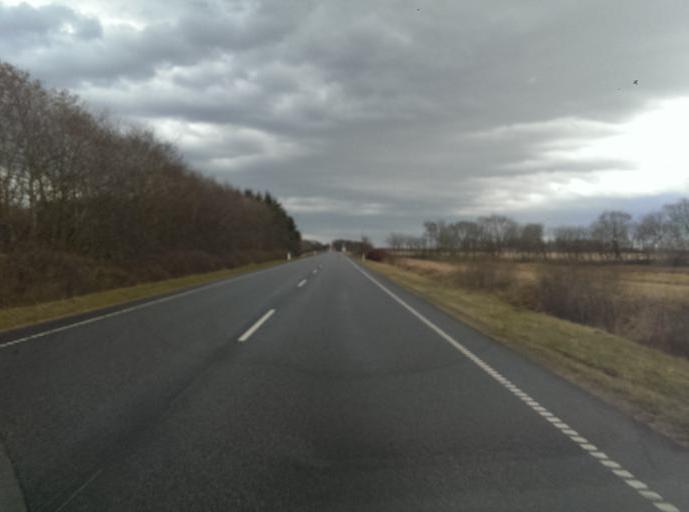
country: DK
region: South Denmark
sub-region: Esbjerg Kommune
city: Tjaereborg
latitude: 55.4995
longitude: 8.6143
